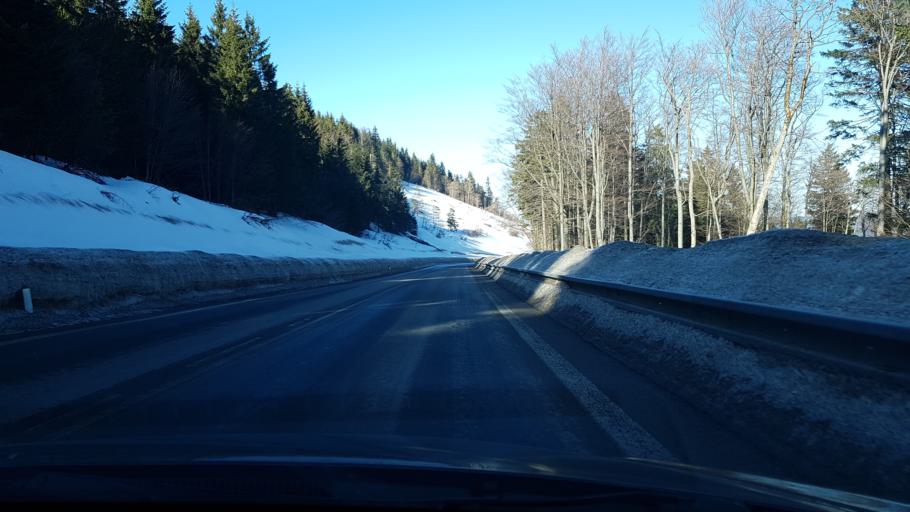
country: CZ
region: Olomoucky
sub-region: Okres Sumperk
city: Loucna nad Desnou
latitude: 50.1282
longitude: 17.1550
